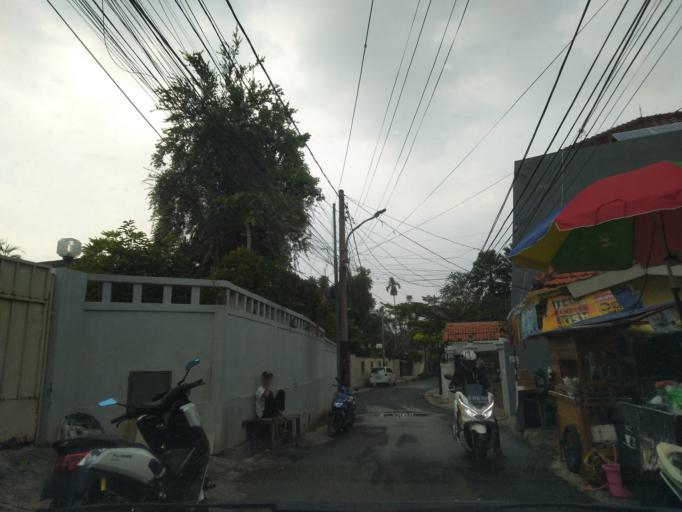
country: ID
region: Jakarta Raya
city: Jakarta
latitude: -6.2606
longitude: 106.8201
